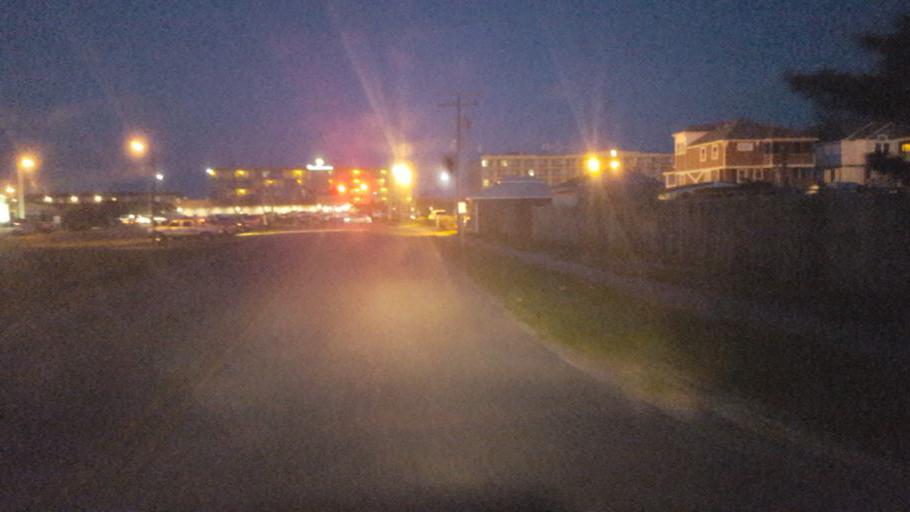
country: US
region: North Carolina
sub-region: Dare County
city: Kill Devil Hills
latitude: 35.9994
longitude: -75.6498
